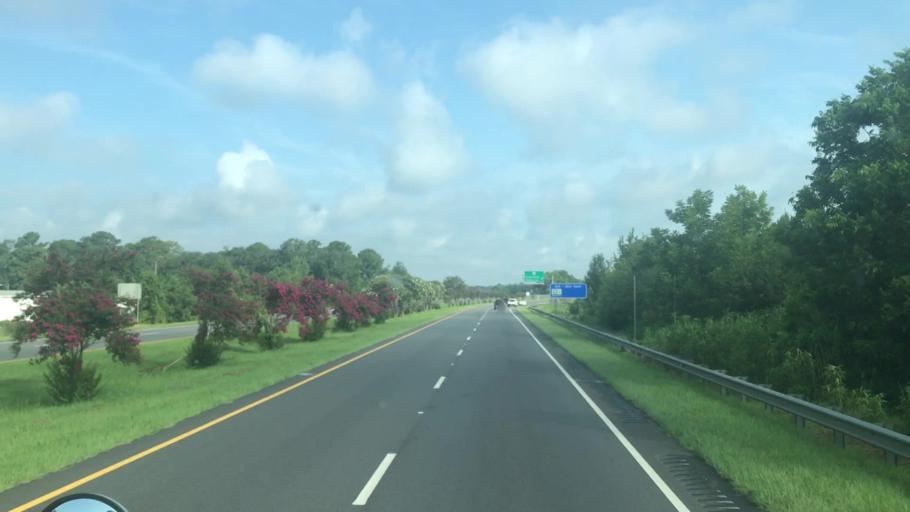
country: US
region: Georgia
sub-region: Decatur County
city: Bainbridge
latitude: 30.9151
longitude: -84.5979
